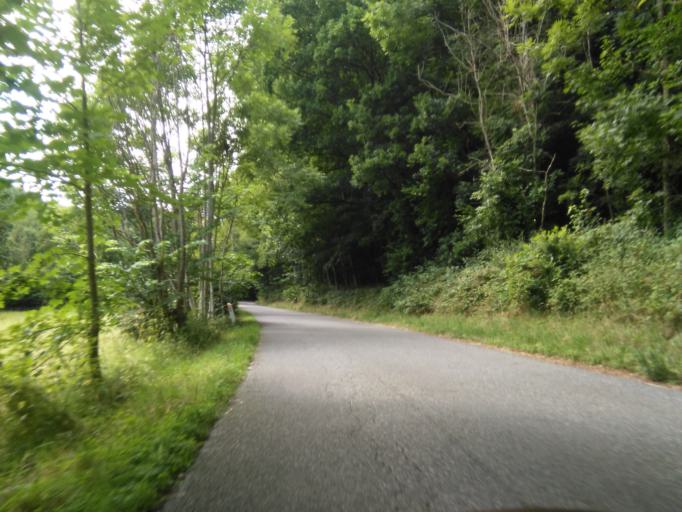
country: DK
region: Central Jutland
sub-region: Skanderborg Kommune
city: Horning
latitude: 56.1077
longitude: 10.0148
